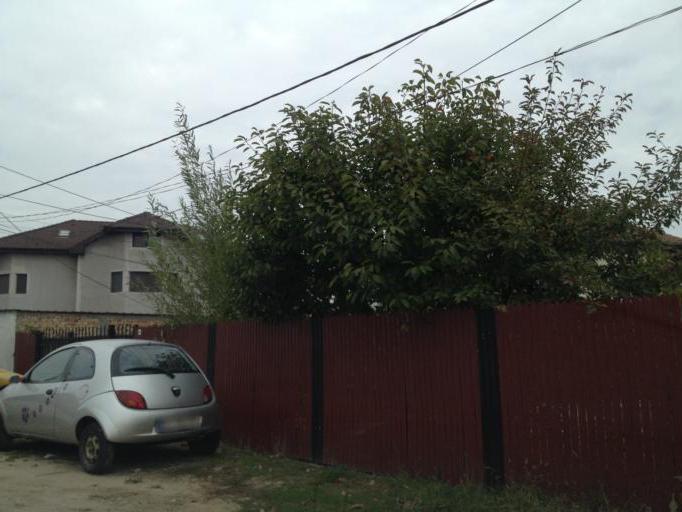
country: RO
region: Dolj
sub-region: Municipiul Craiova
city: Facai
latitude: 44.2924
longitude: 23.8090
